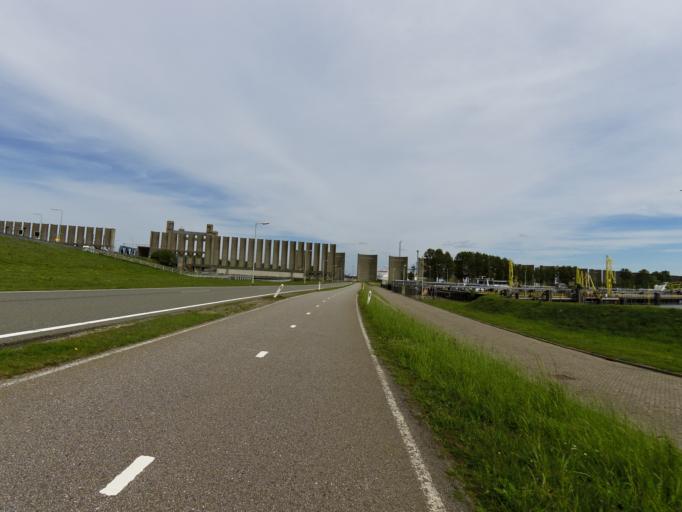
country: NL
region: South Holland
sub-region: Gemeente Maassluis
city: Maassluis
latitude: 51.9000
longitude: 4.2210
